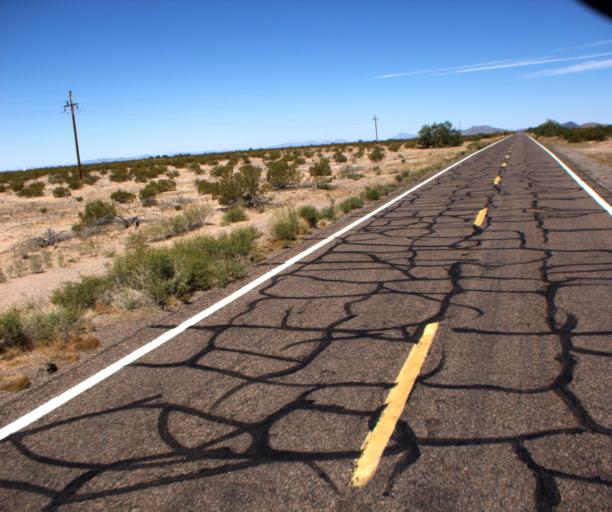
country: US
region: Arizona
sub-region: Pima County
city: Ajo
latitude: 32.6401
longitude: -112.8632
